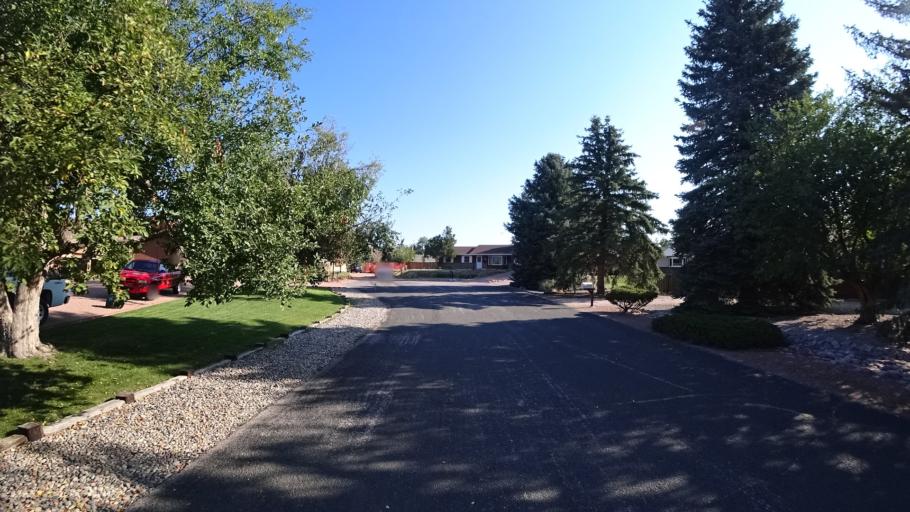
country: US
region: Colorado
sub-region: El Paso County
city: Air Force Academy
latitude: 38.9316
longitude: -104.7908
